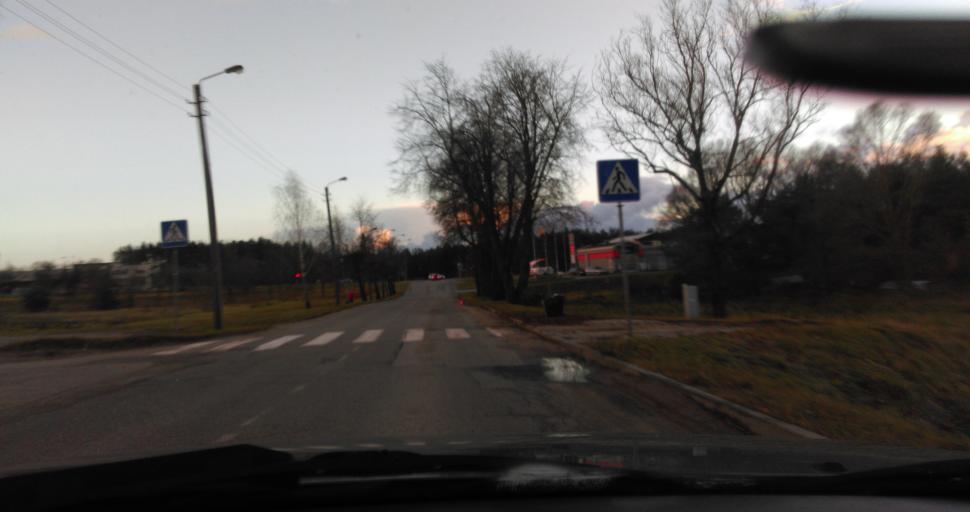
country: LT
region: Utenos apskritis
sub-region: Utena
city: Utena
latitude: 55.5064
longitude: 25.6211
